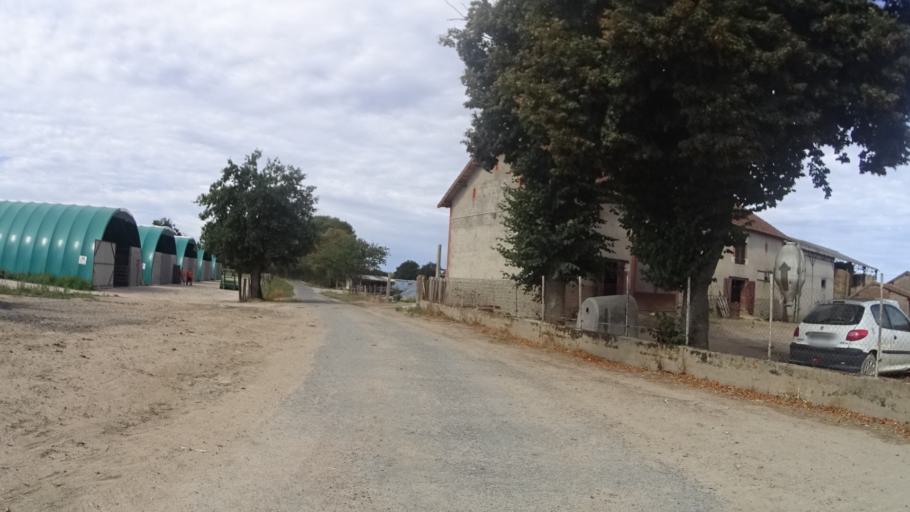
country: FR
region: Auvergne
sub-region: Departement de l'Allier
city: Beaulon
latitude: 46.6479
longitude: 3.6783
